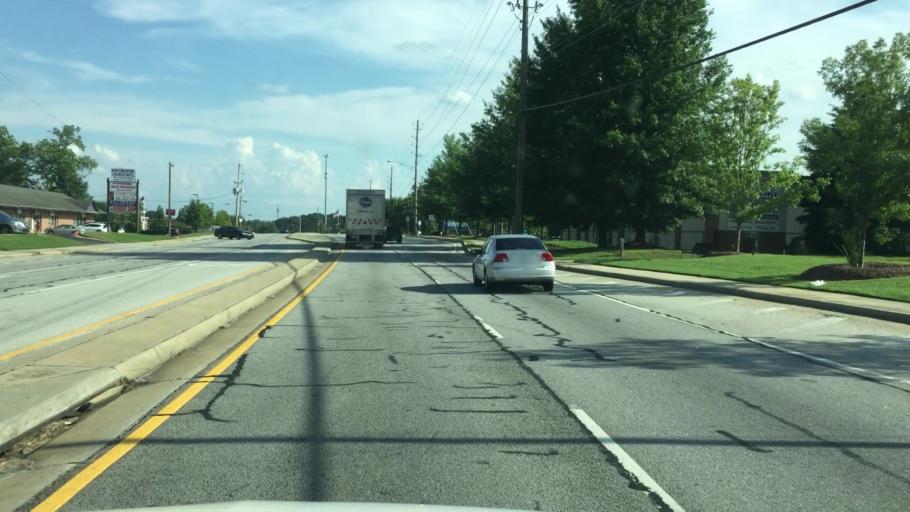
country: US
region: Georgia
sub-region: Gwinnett County
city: Snellville
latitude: 33.8078
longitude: -84.0434
